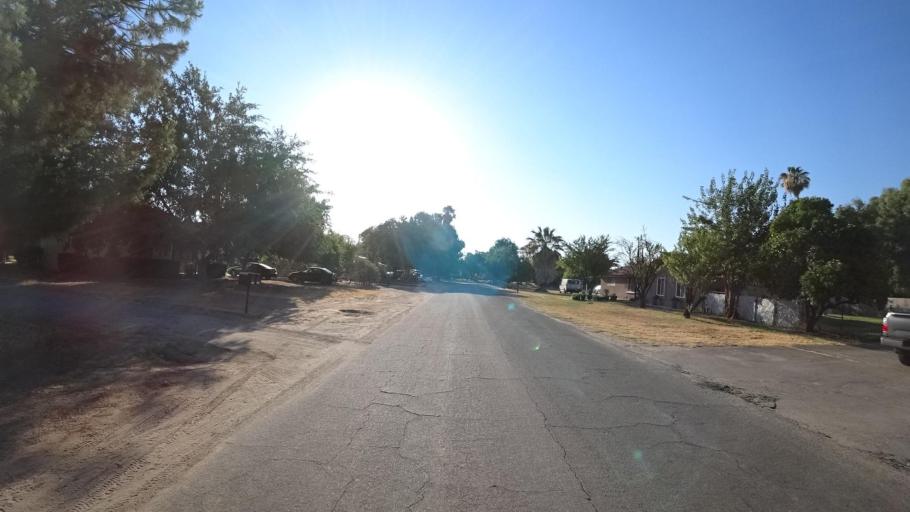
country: US
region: California
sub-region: Fresno County
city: Sunnyside
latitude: 36.7383
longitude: -119.7055
